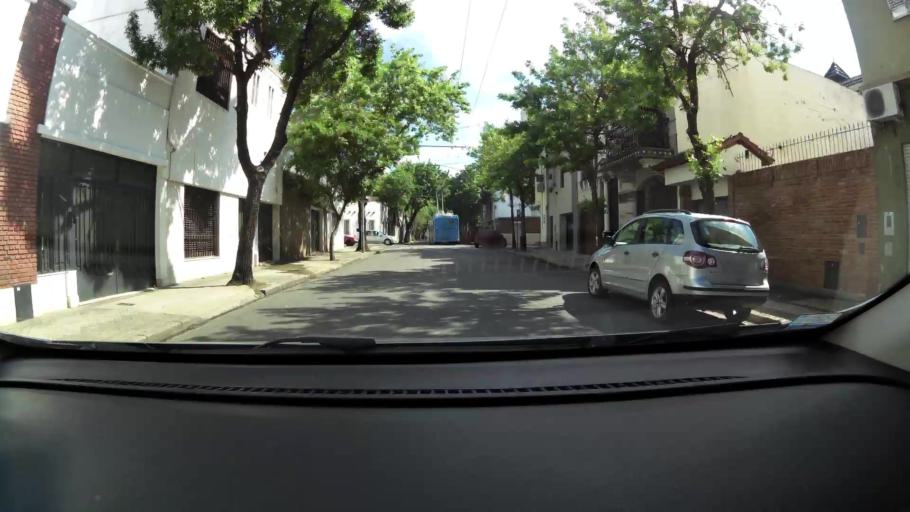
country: AR
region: Santa Fe
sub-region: Departamento de Rosario
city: Rosario
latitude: -32.9590
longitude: -60.6267
